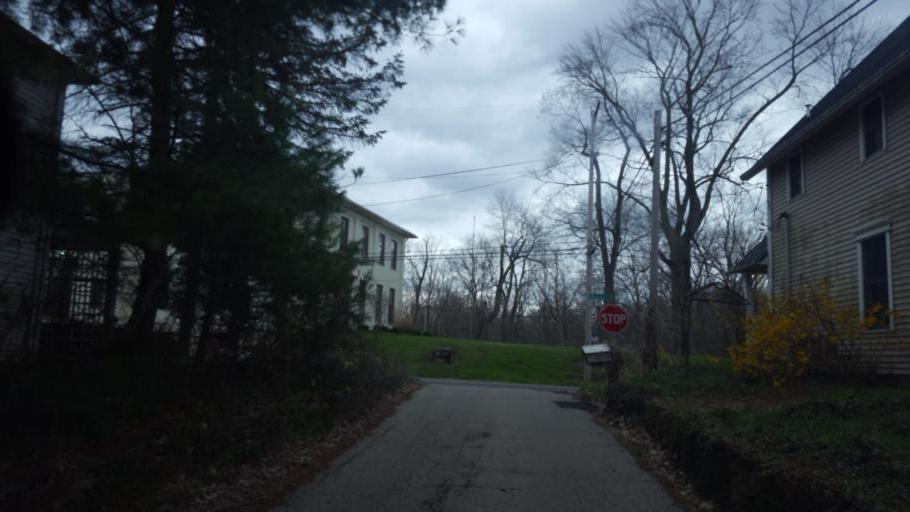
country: US
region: Ohio
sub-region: Delaware County
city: Sunbury
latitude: 40.2166
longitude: -82.8803
